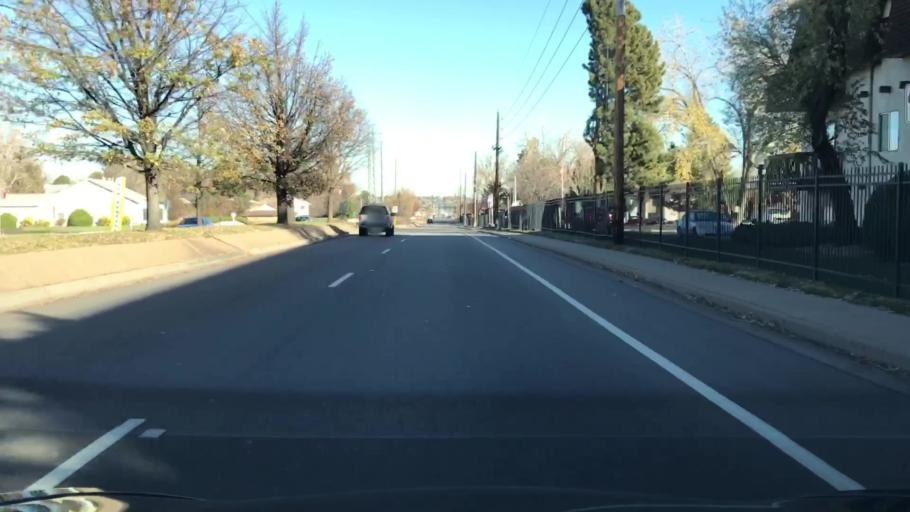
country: US
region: Colorado
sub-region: Arapahoe County
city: Glendale
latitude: 39.6719
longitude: -104.9035
